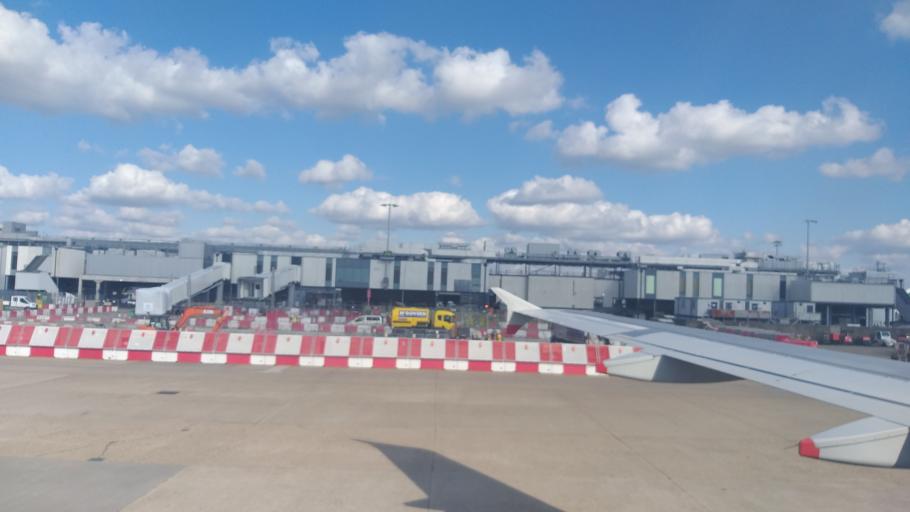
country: GB
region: England
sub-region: Greater London
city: West Drayton
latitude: 51.4680
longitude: -0.4643
